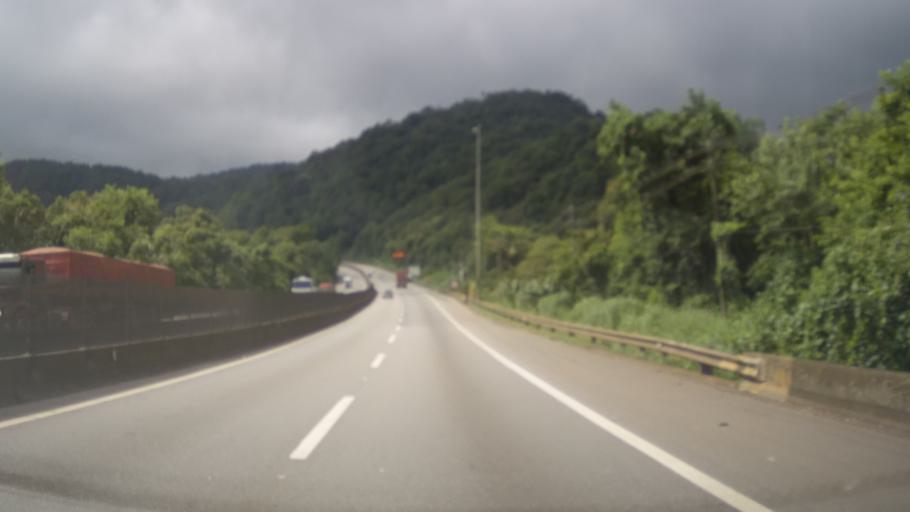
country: BR
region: Sao Paulo
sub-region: Cubatao
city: Cubatao
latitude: -23.8679
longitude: -46.3456
